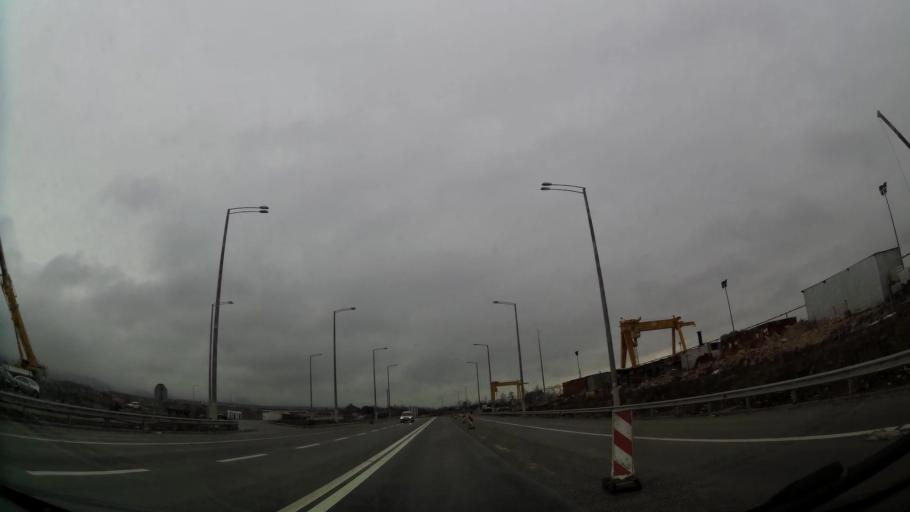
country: XK
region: Ferizaj
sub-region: Komuna e Kacanikut
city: Kacanik
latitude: 42.2757
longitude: 21.2153
